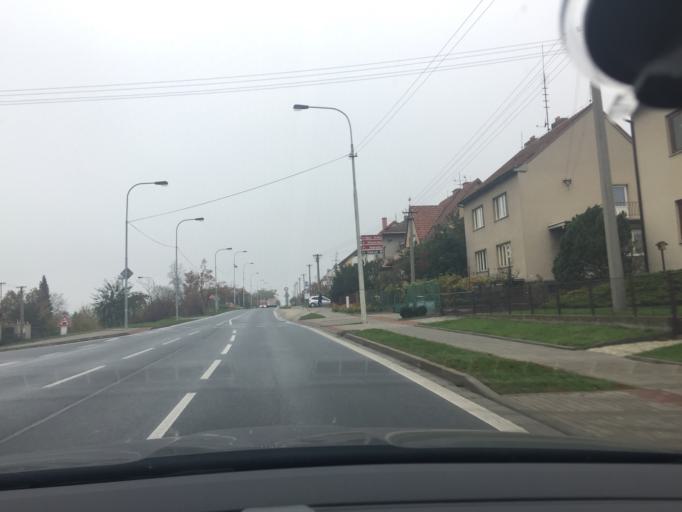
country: CZ
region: South Moravian
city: Rousinov
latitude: 49.1996
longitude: 16.8719
